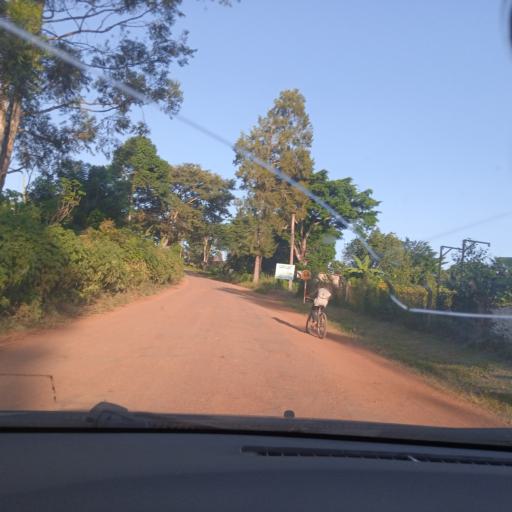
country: UG
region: Central Region
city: Masaka
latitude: -0.3354
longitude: 31.7599
